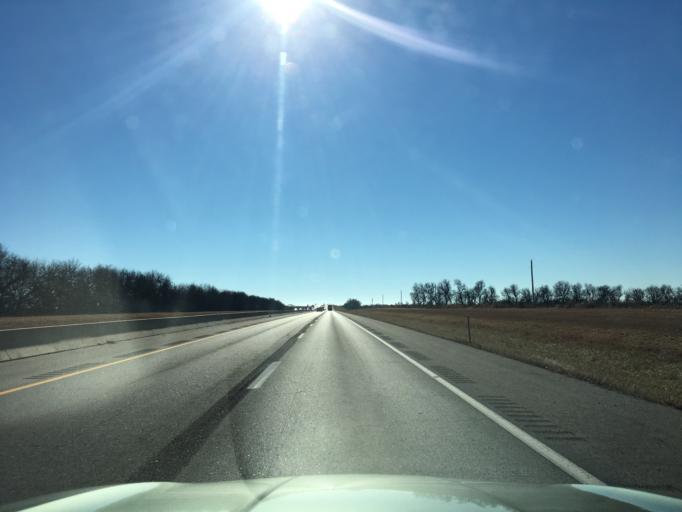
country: US
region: Kansas
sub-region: Sumner County
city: Wellington
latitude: 37.0820
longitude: -97.3386
